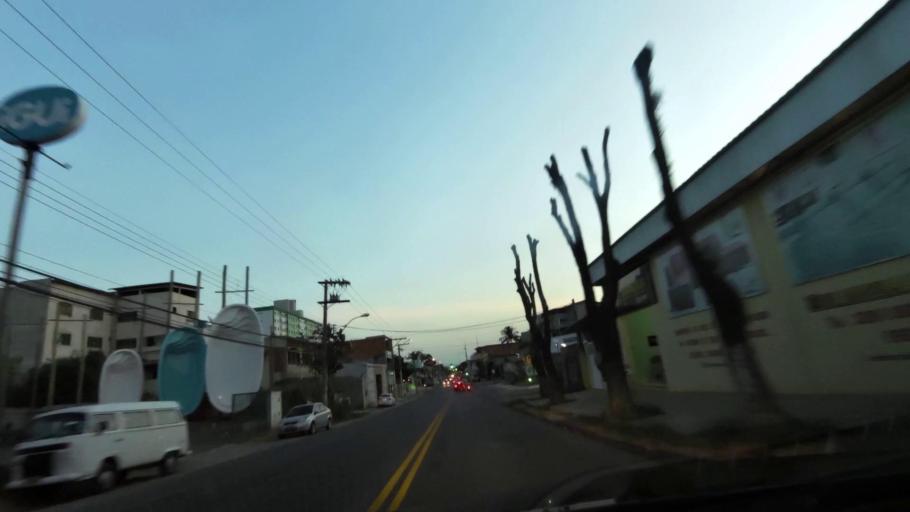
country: BR
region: Espirito Santo
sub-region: Guarapari
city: Guarapari
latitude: -20.6387
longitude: -40.4822
